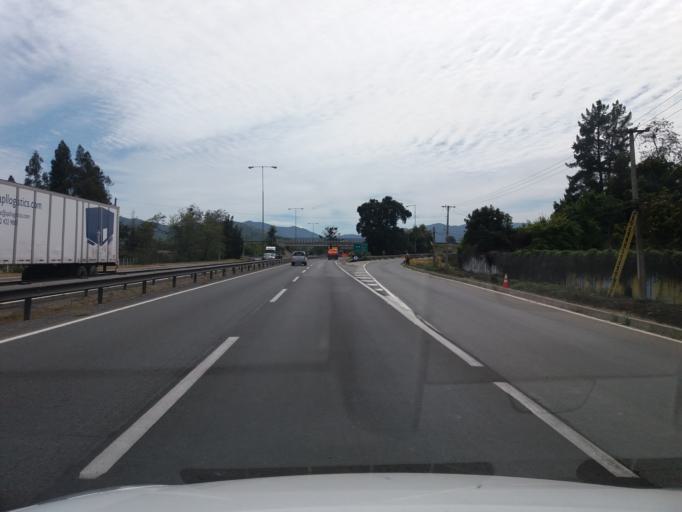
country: CL
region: Valparaiso
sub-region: Provincia de Quillota
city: Hacienda La Calera
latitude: -32.7247
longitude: -71.2030
